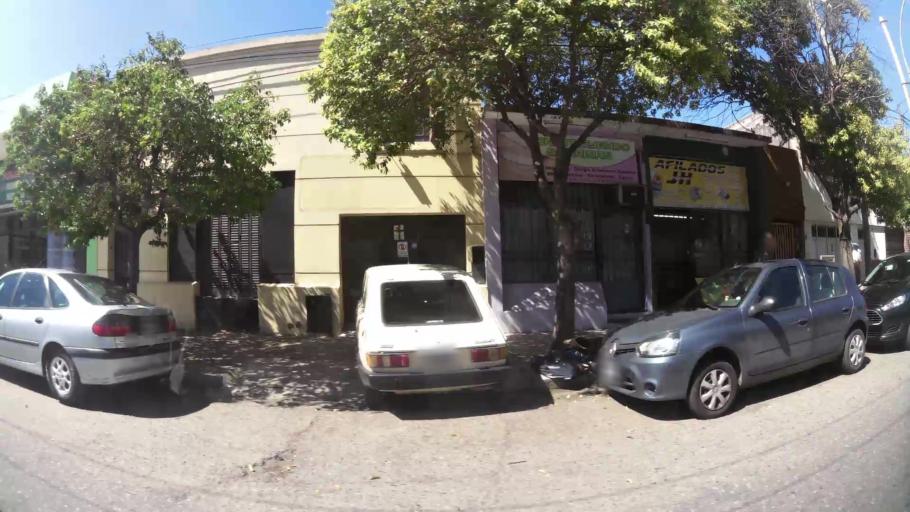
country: AR
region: Cordoba
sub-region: Departamento de Capital
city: Cordoba
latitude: -31.4228
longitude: -64.1549
